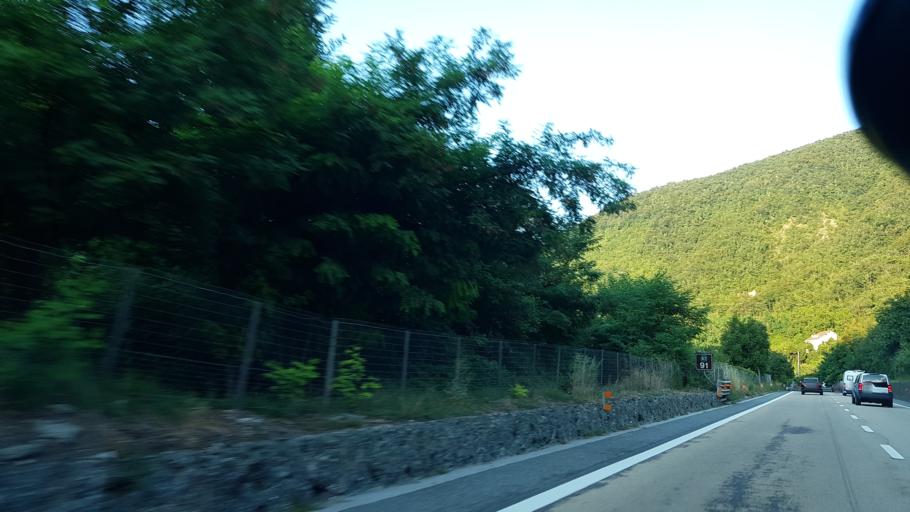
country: IT
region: Liguria
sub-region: Provincia di Genova
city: Isola del Cantone
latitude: 44.6583
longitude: 8.9226
